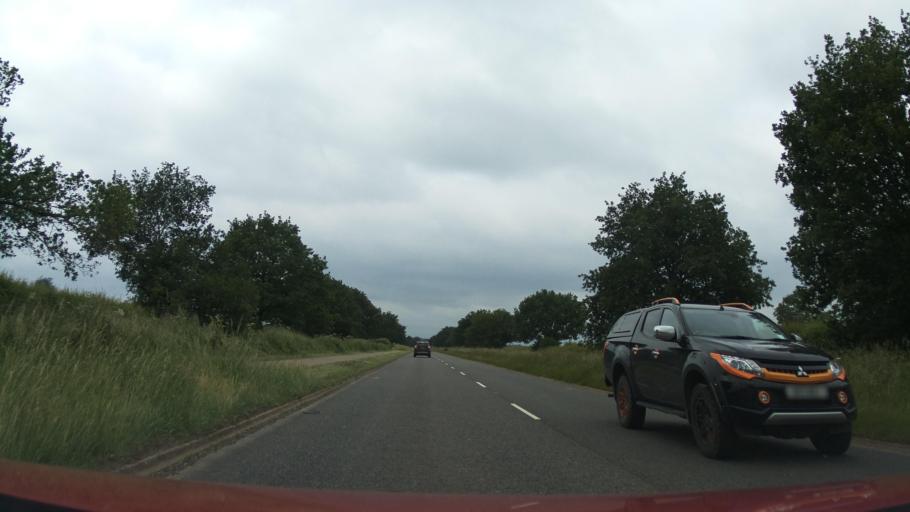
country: GB
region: England
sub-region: District of Rutland
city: Burley
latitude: 52.6727
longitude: -0.6940
